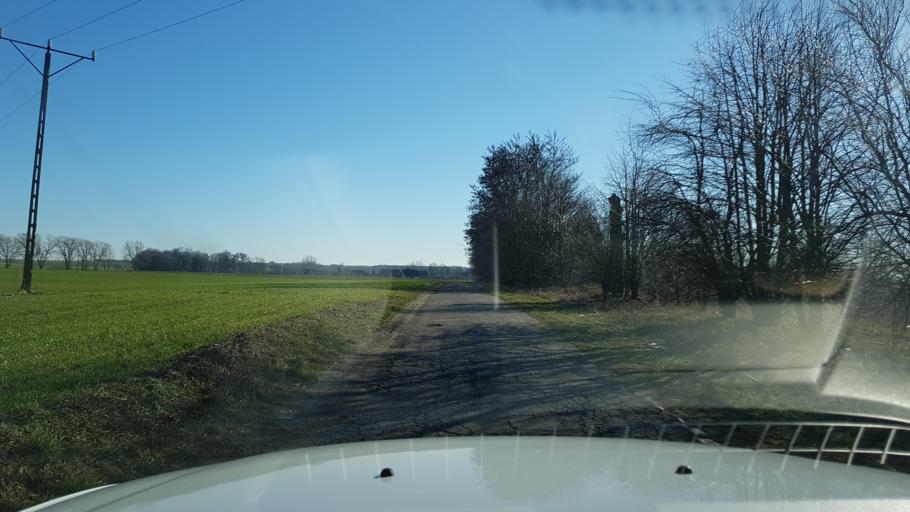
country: PL
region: West Pomeranian Voivodeship
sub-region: Powiat pyrzycki
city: Przelewice
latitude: 53.0295
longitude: 15.0705
